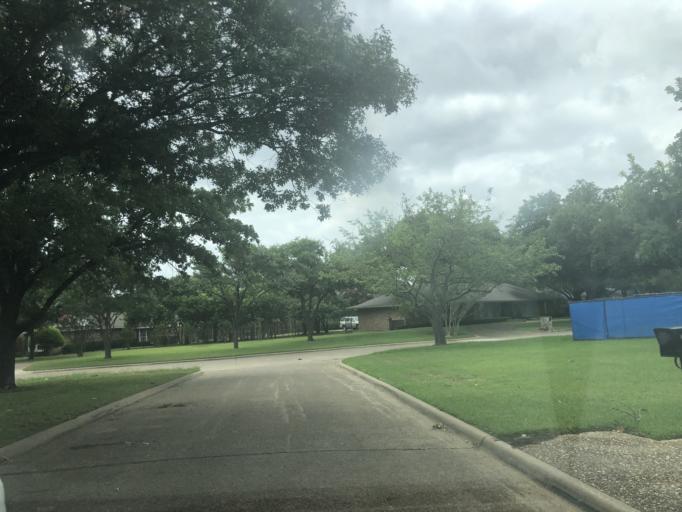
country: US
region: Texas
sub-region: Dallas County
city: University Park
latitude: 32.8885
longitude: -96.8319
